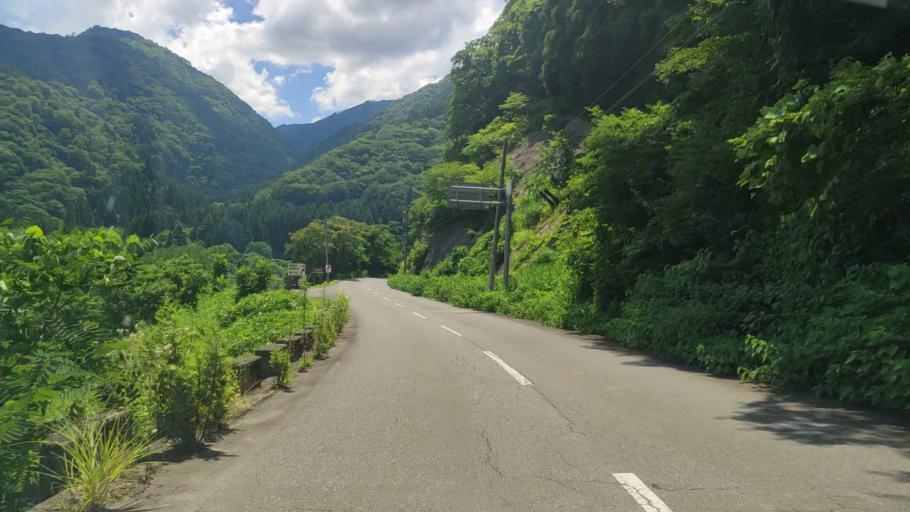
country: JP
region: Fukui
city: Ono
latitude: 35.8763
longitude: 136.5061
